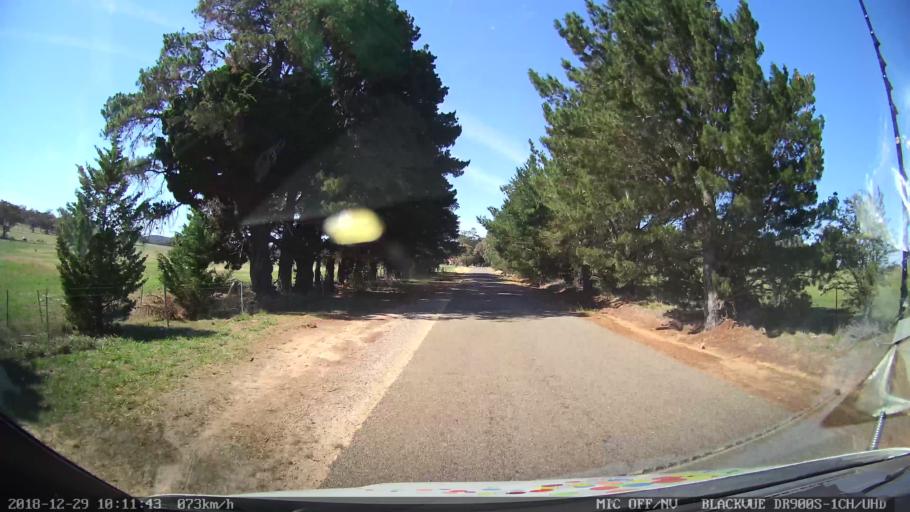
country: AU
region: New South Wales
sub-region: Yass Valley
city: Gundaroo
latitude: -34.8866
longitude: 149.4512
